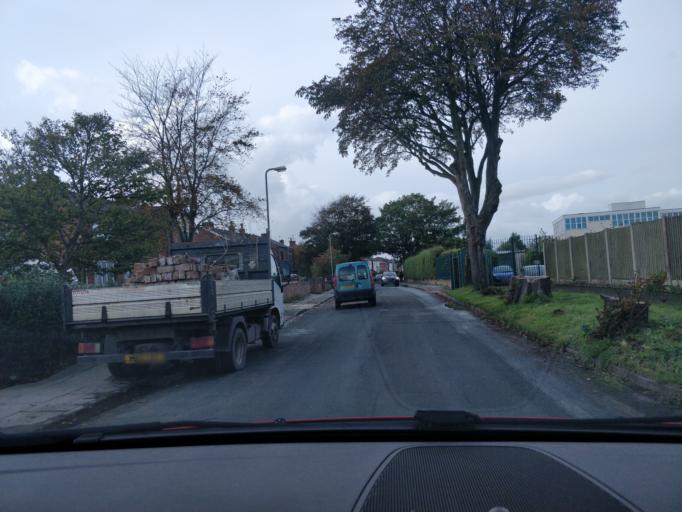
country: GB
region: England
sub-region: Sefton
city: Southport
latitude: 53.6255
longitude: -3.0017
